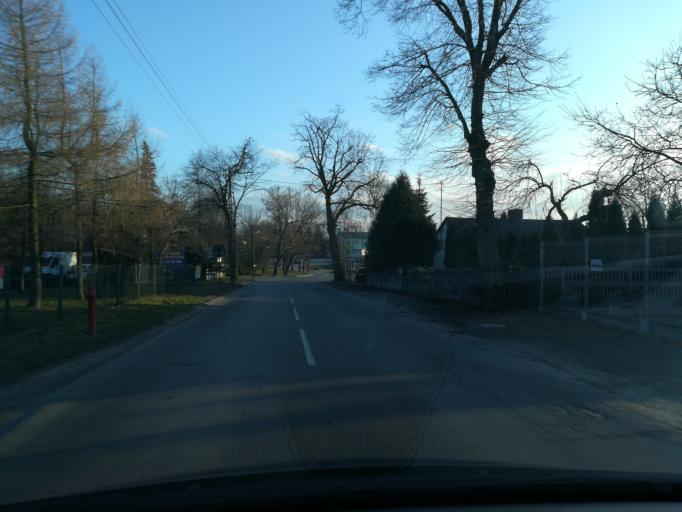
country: PL
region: Lodz Voivodeship
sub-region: Piotrkow Trybunalski
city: Piotrkow Trybunalski
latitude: 51.4065
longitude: 19.6471
